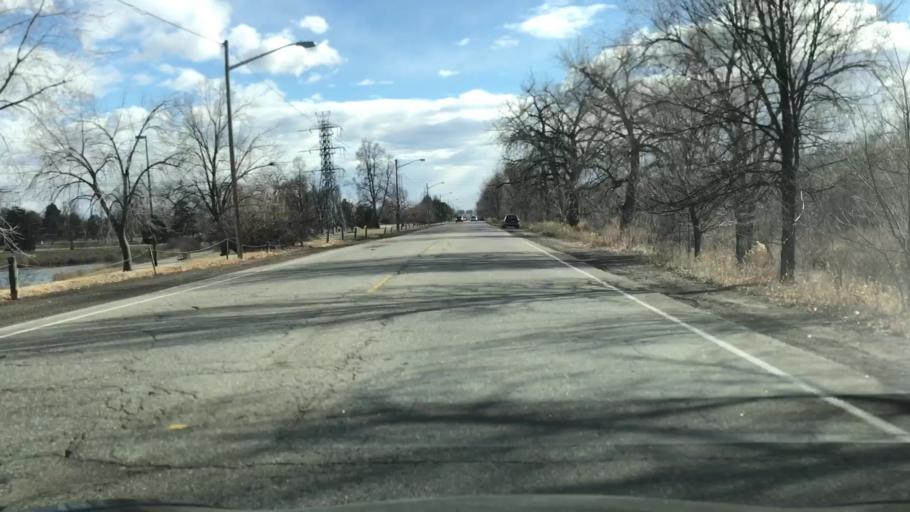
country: US
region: Colorado
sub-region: Arapahoe County
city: Glendale
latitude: 39.6955
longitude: -104.9201
